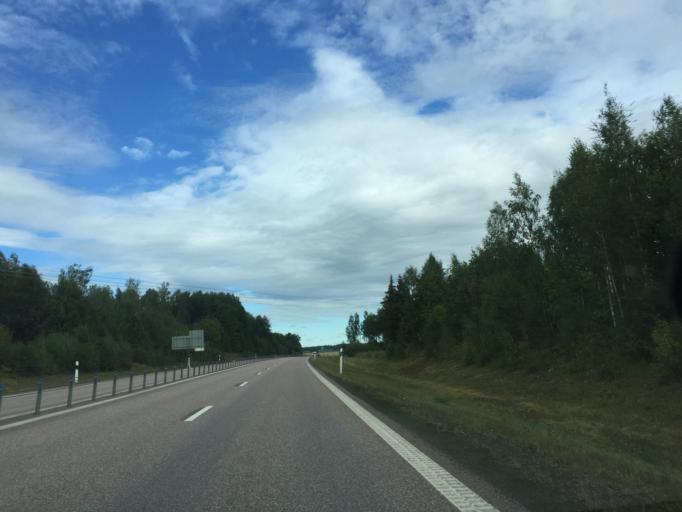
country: SE
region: Vaestmanland
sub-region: Arboga Kommun
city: Arboga
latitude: 59.4153
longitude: 15.8853
